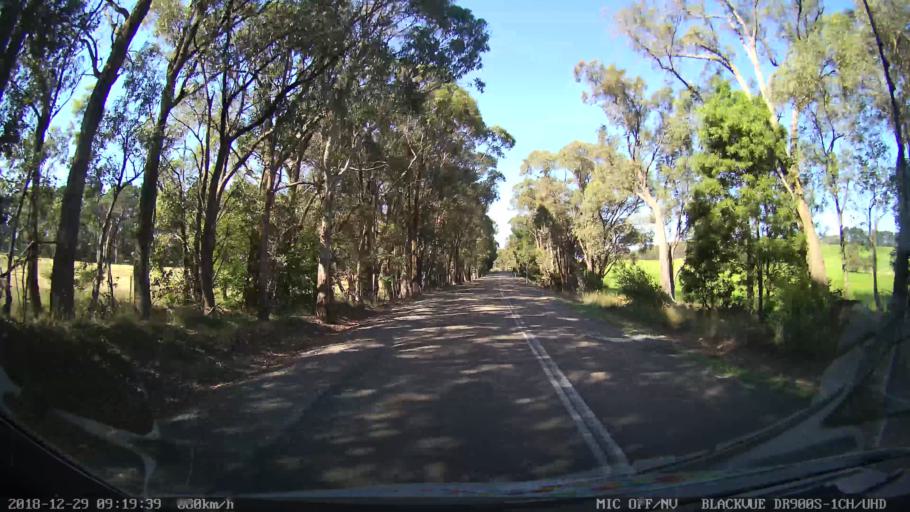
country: AU
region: New South Wales
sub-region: Upper Lachlan Shire
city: Crookwell
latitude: -34.4838
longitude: 149.4277
